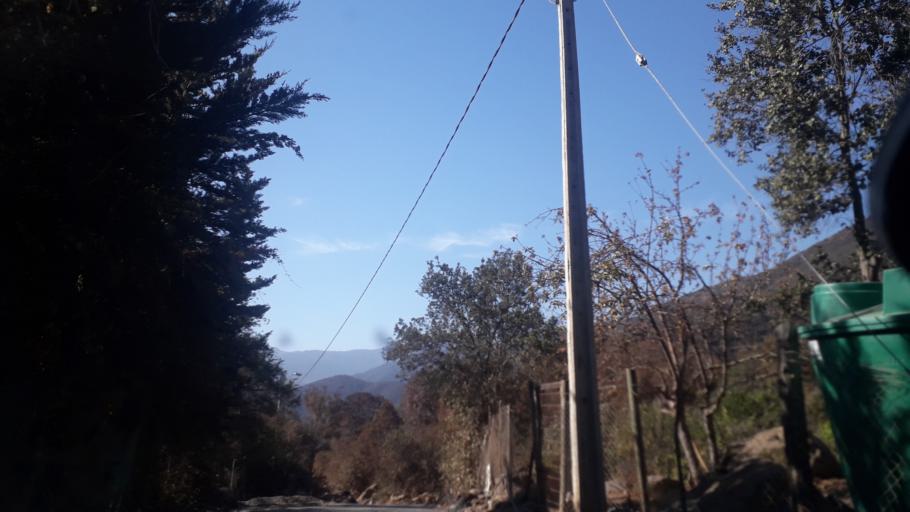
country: CL
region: Valparaiso
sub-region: Provincia de Marga Marga
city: Limache
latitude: -33.0812
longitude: -71.1000
